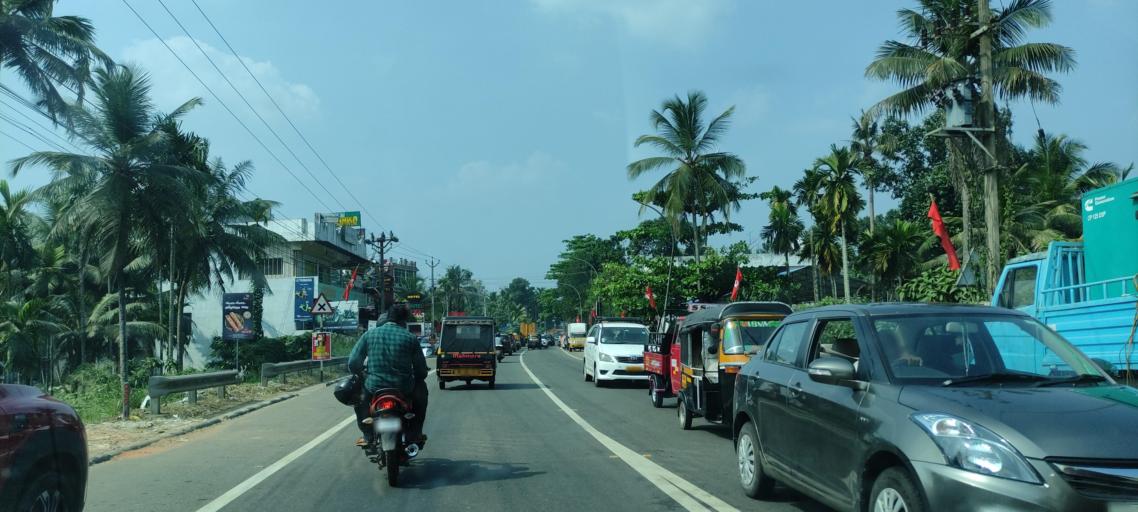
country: IN
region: Kerala
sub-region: Pattanamtitta
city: Adur
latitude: 9.1470
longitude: 76.7313
